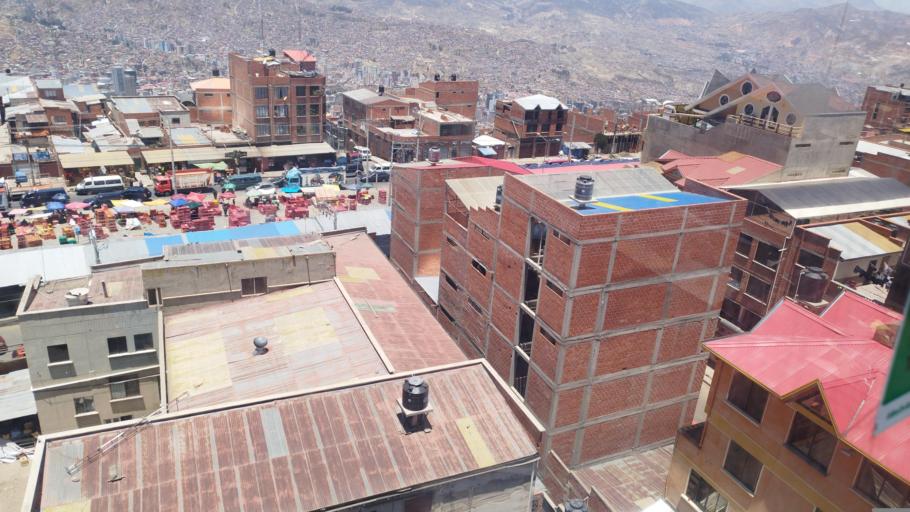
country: BO
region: La Paz
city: La Paz
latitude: -16.5096
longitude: -68.1559
